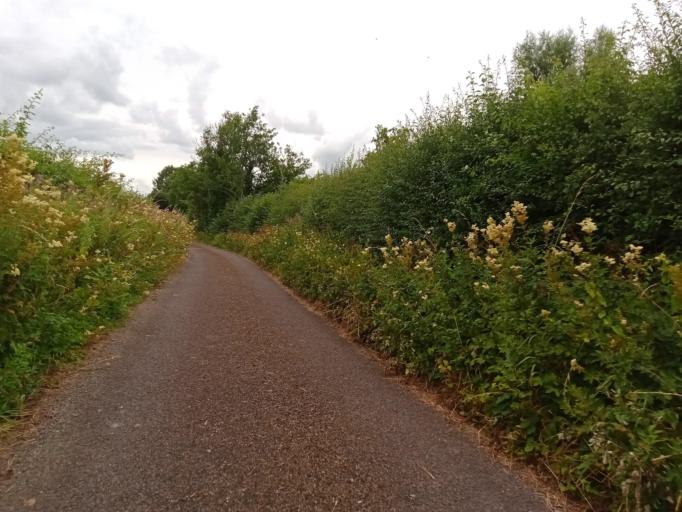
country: IE
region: Leinster
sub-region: Kilkenny
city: Callan
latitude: 52.5400
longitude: -7.4239
